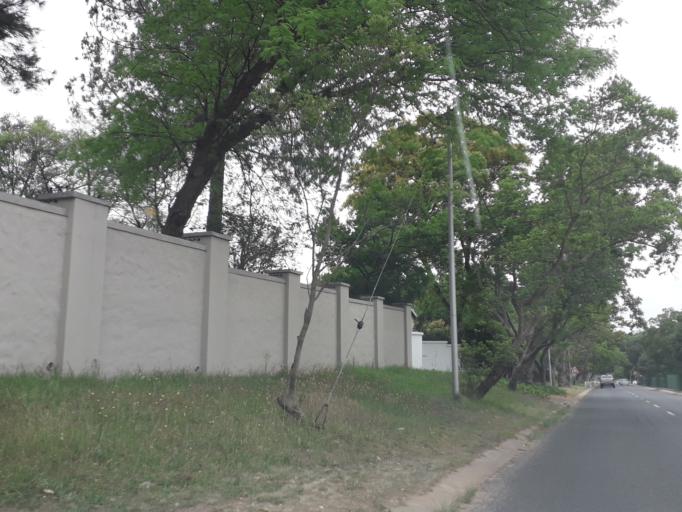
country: ZA
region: Gauteng
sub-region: City of Johannesburg Metropolitan Municipality
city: Midrand
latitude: -26.0460
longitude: 28.0414
